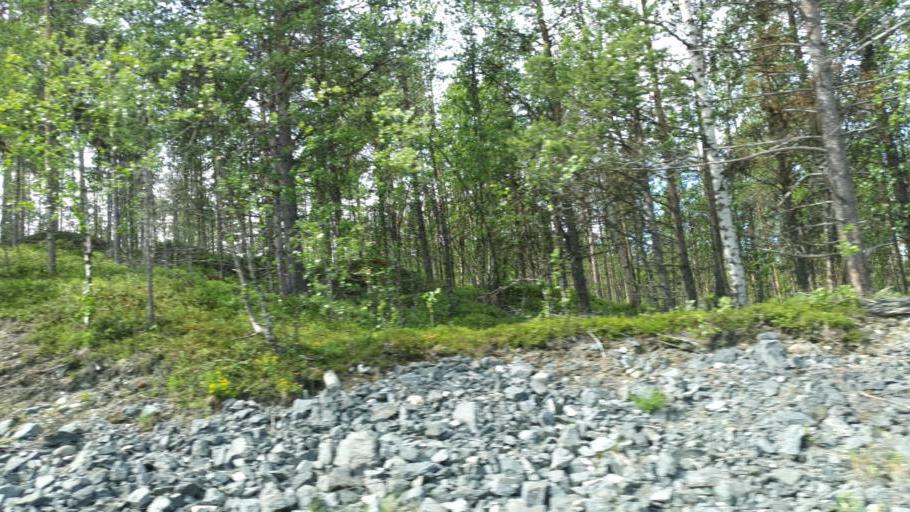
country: NO
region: Oppland
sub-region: Vaga
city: Vagamo
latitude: 61.7025
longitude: 9.0586
